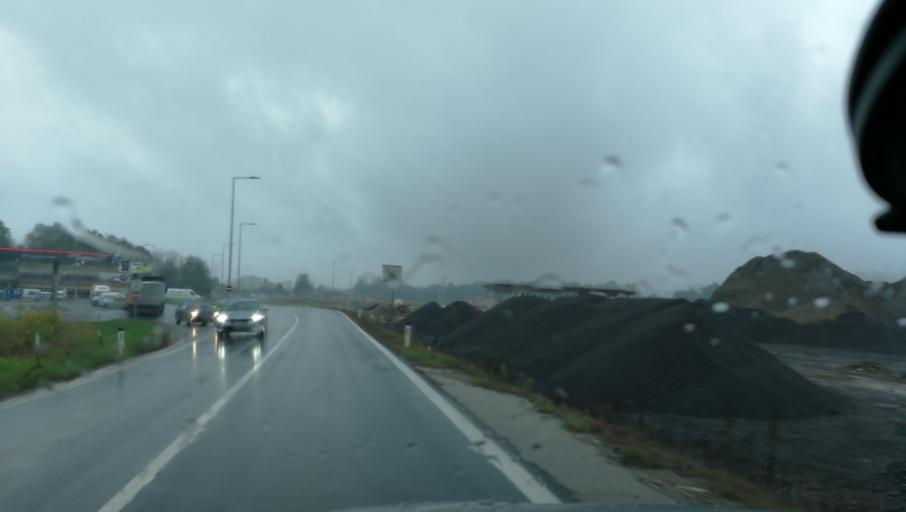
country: AT
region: Styria
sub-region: Politischer Bezirk Leibnitz
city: Spielfeld
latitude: 46.7199
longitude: 15.6543
